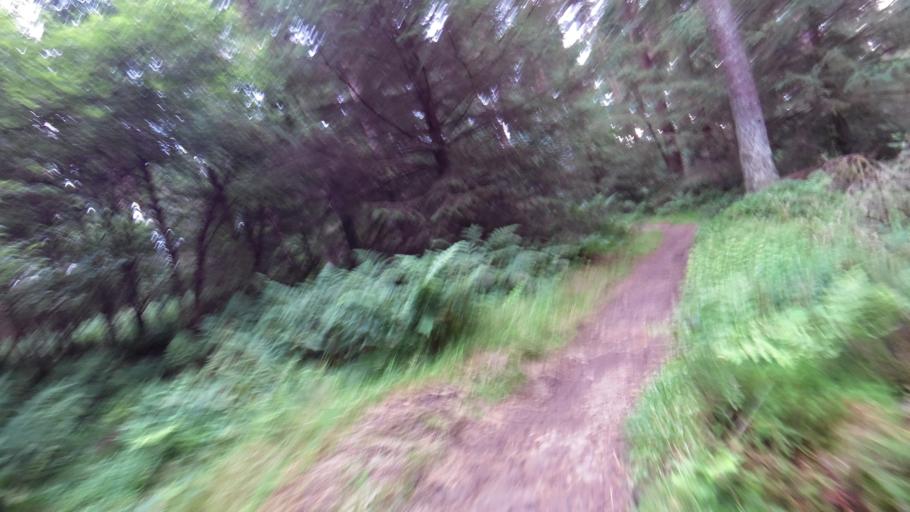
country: GB
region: England
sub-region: North Yorkshire
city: Thornton Dale
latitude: 54.2927
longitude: -0.6710
